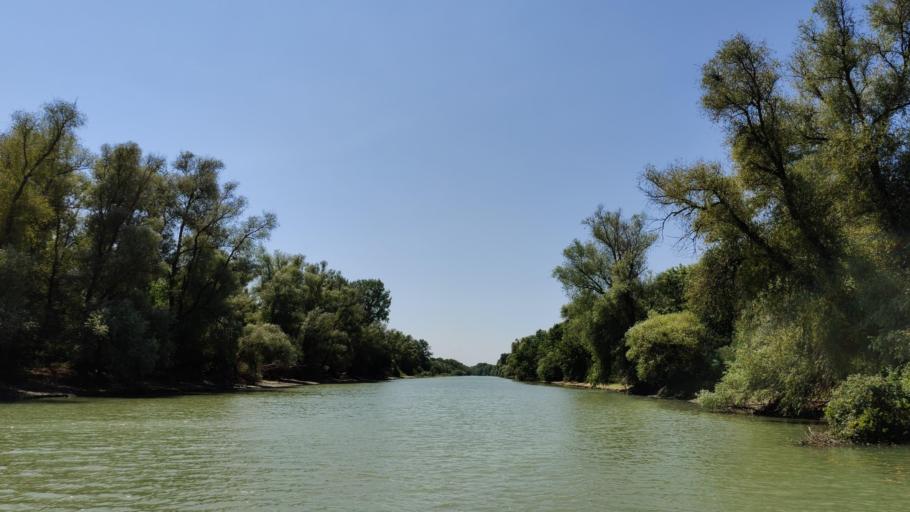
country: RO
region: Tulcea
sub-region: Comuna Nufaru
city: Malcoci
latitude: 45.2168
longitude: 28.8717
